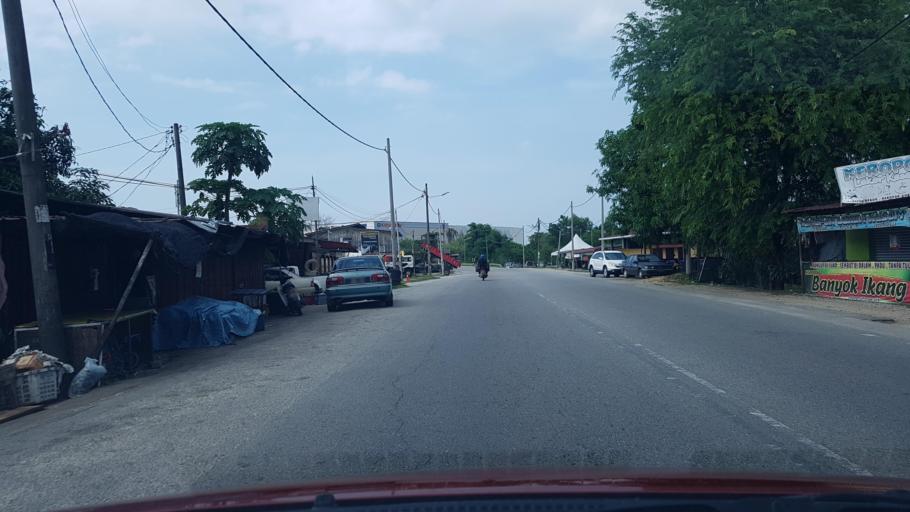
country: MY
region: Terengganu
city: Kuala Terengganu
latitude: 5.3525
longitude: 103.0938
